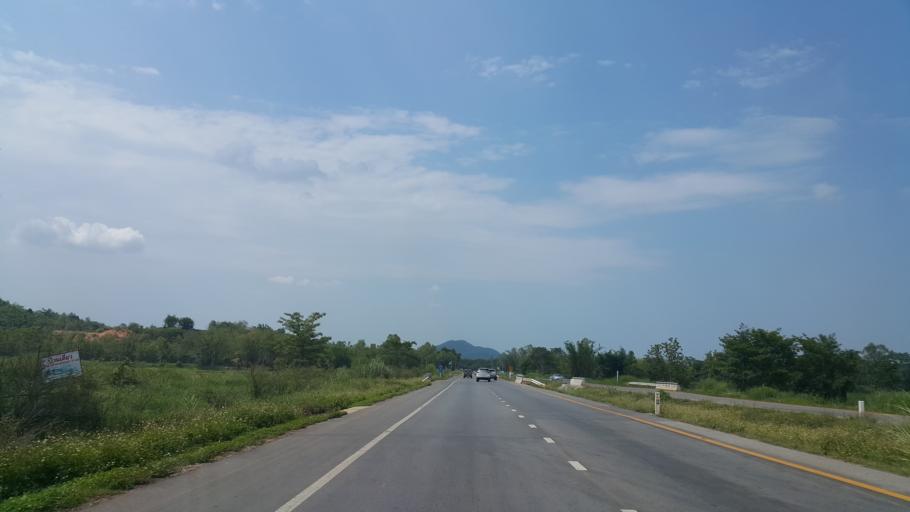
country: TH
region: Chiang Rai
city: Chiang Rai
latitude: 19.9808
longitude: 99.8898
